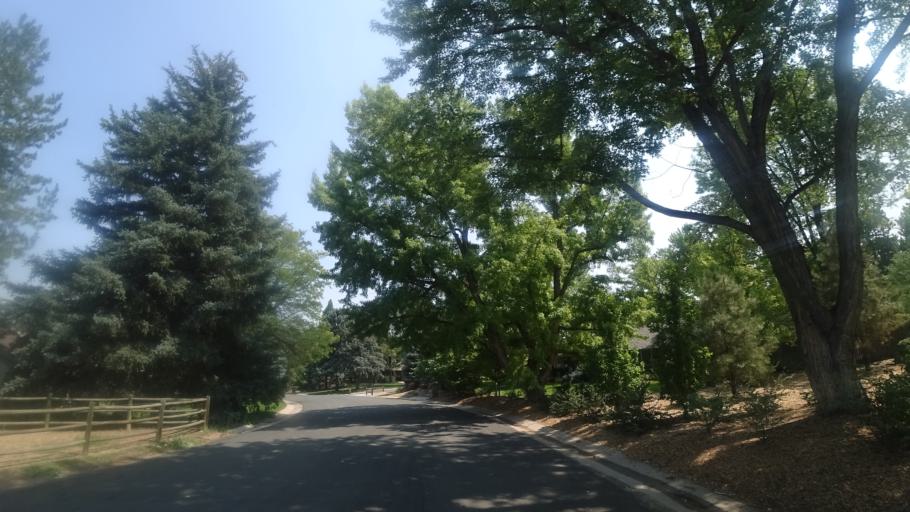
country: US
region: Colorado
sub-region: Arapahoe County
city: Cherry Hills Village
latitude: 39.6275
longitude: -104.9678
